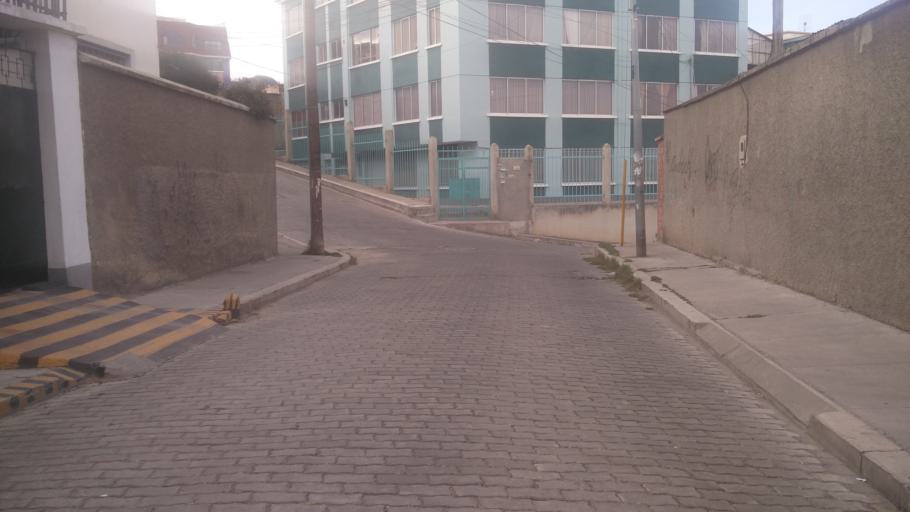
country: BO
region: La Paz
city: La Paz
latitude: -16.5113
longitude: -68.1321
